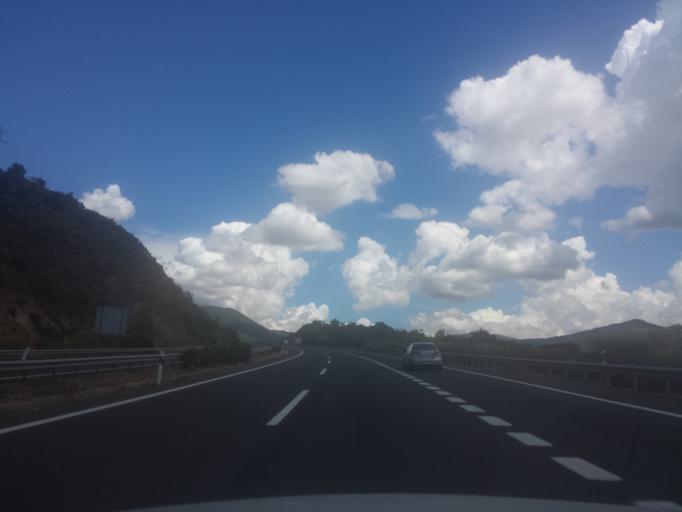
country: ES
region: Extremadura
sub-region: Provincia de Caceres
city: Aldeanueva del Camino
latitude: 40.2794
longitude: -5.9029
